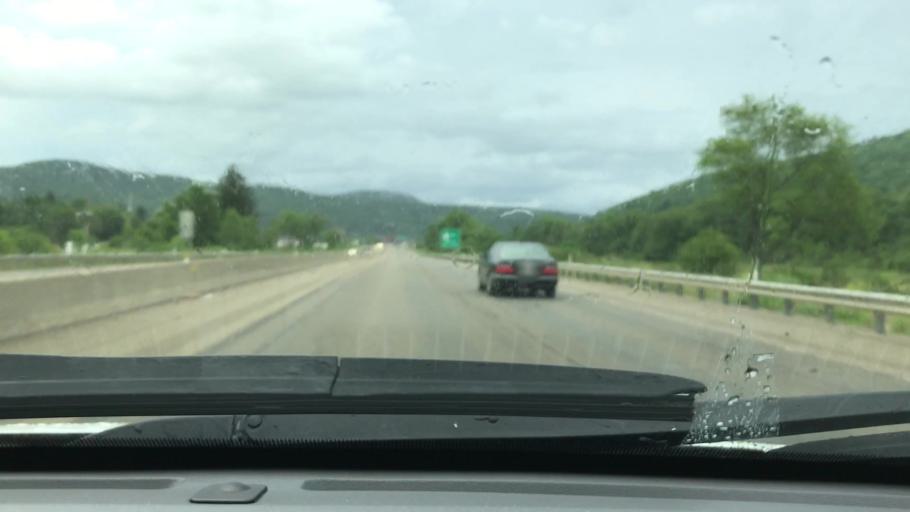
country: US
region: Pennsylvania
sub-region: McKean County
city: Bradford
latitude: 41.9431
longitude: -78.6489
